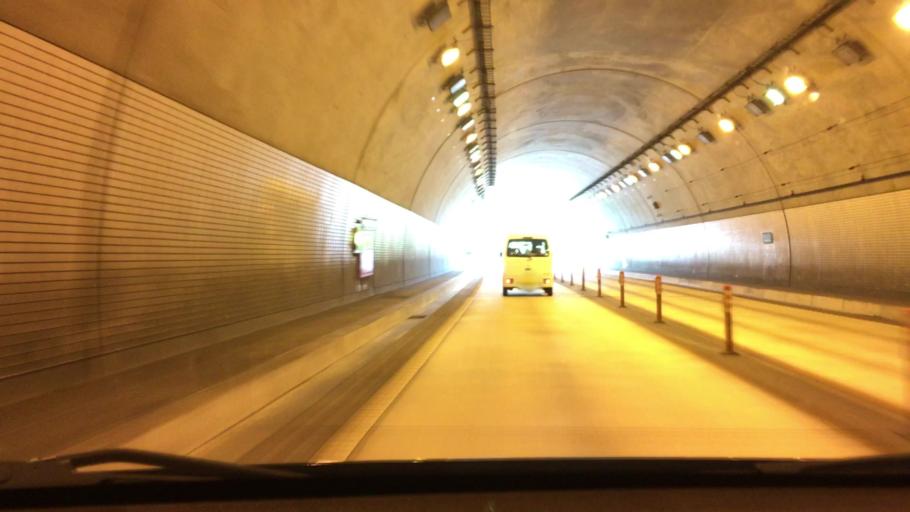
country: JP
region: Nagasaki
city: Sasebo
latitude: 33.1011
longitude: 129.7795
